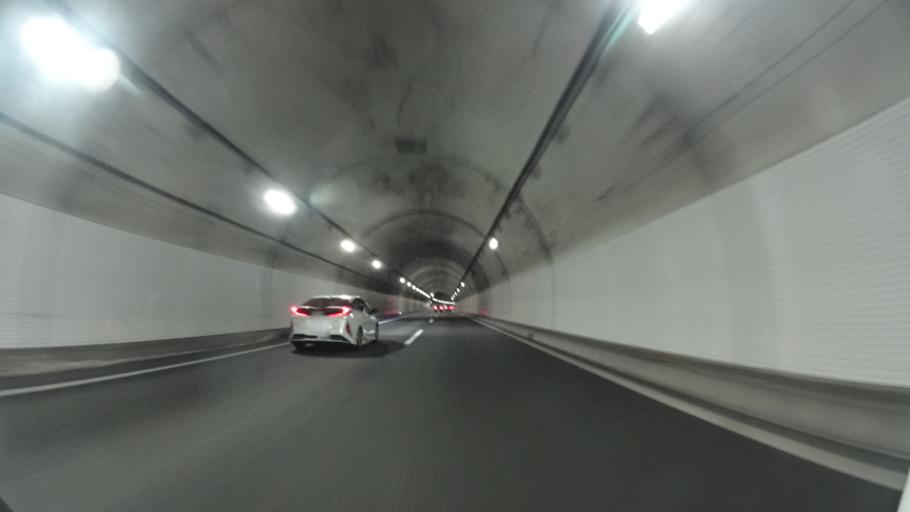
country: JP
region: Ehime
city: Saijo
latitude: 33.8942
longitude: 133.1984
